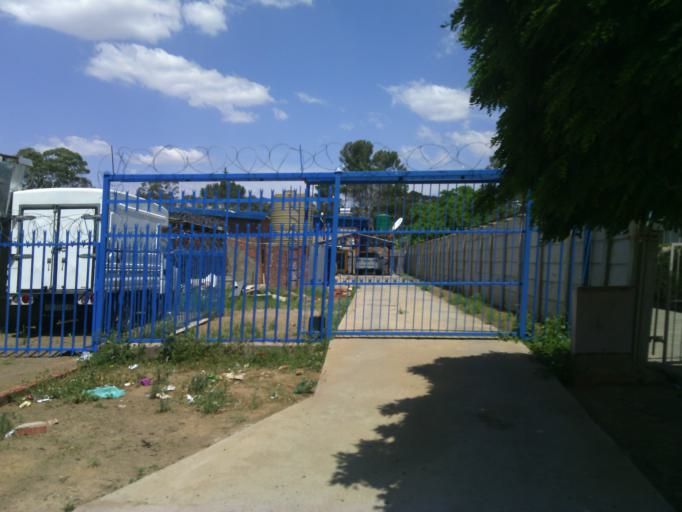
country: ZA
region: Orange Free State
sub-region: Xhariep District Municipality
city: Dewetsdorp
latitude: -29.5843
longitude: 26.6656
